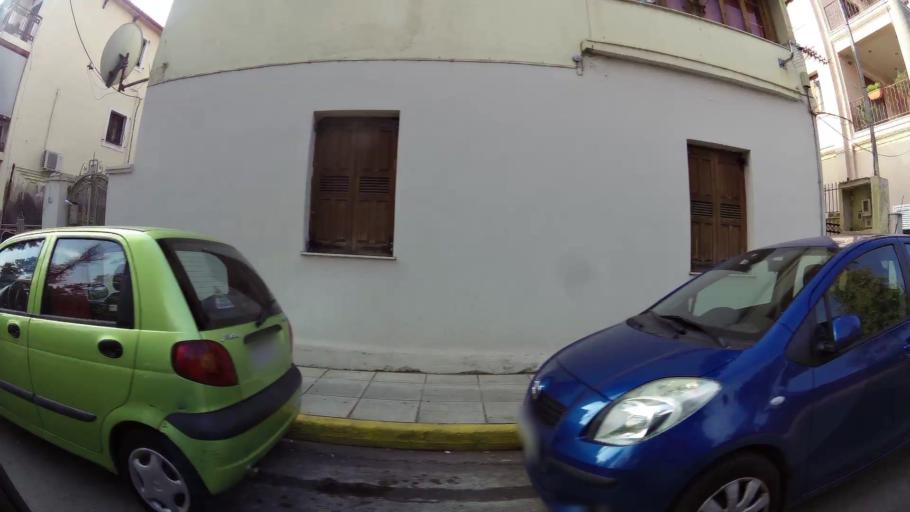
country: GR
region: Attica
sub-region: Nomarchia Athinas
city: Nea Filadelfeia
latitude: 38.0347
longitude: 23.7411
